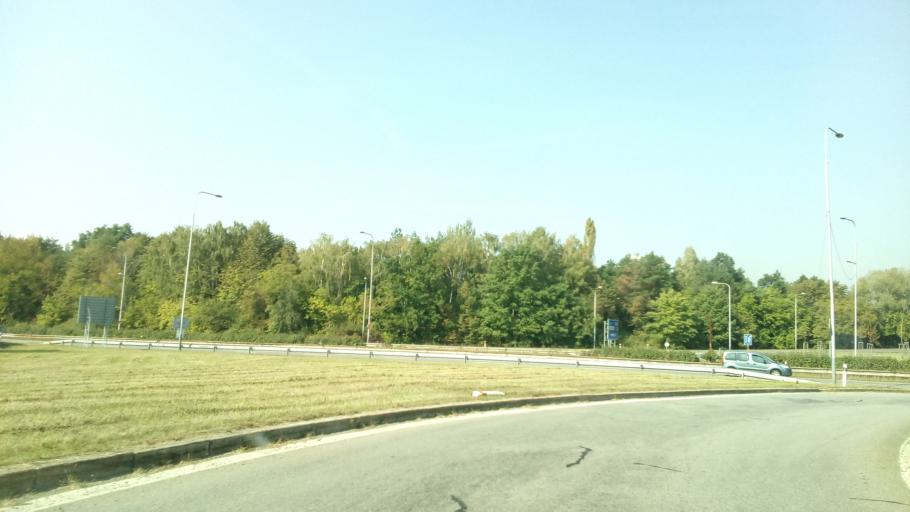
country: CZ
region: Moravskoslezsky
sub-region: Okres Ostrava-Mesto
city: Ostrava
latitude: 49.7976
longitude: 18.2458
